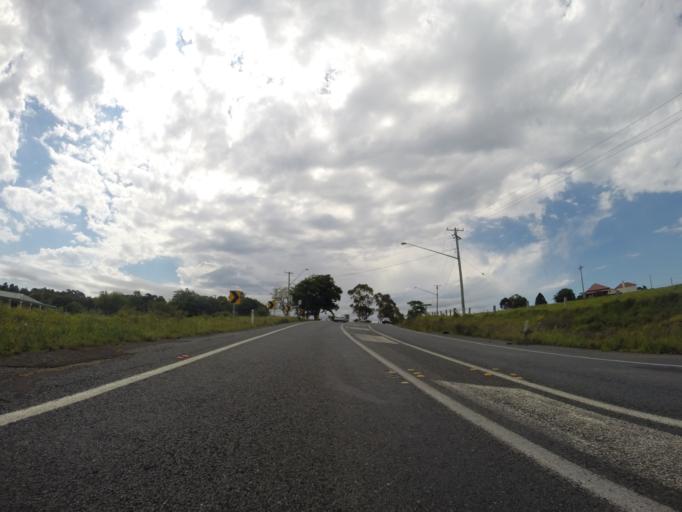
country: AU
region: New South Wales
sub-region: Shoalhaven Shire
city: Milton
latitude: -35.2946
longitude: 150.4225
